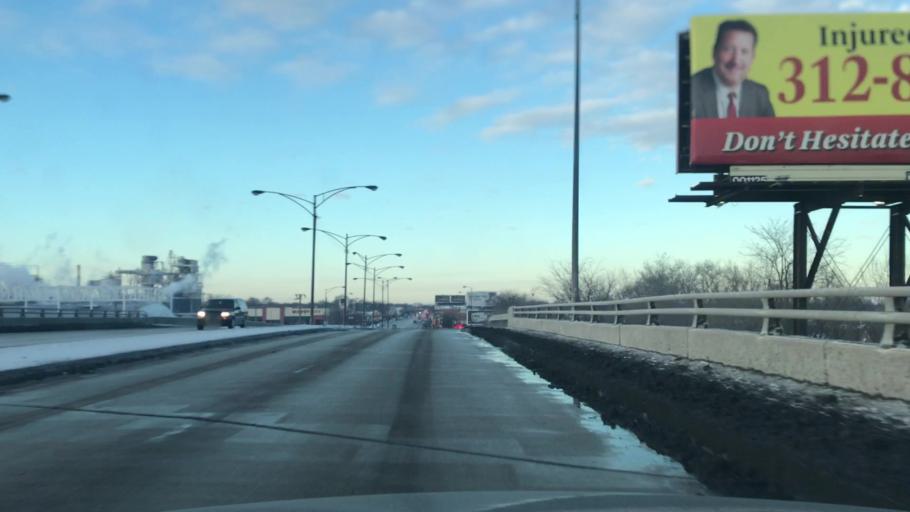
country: US
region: Illinois
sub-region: Cook County
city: Hometown
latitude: 41.7618
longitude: -87.7222
